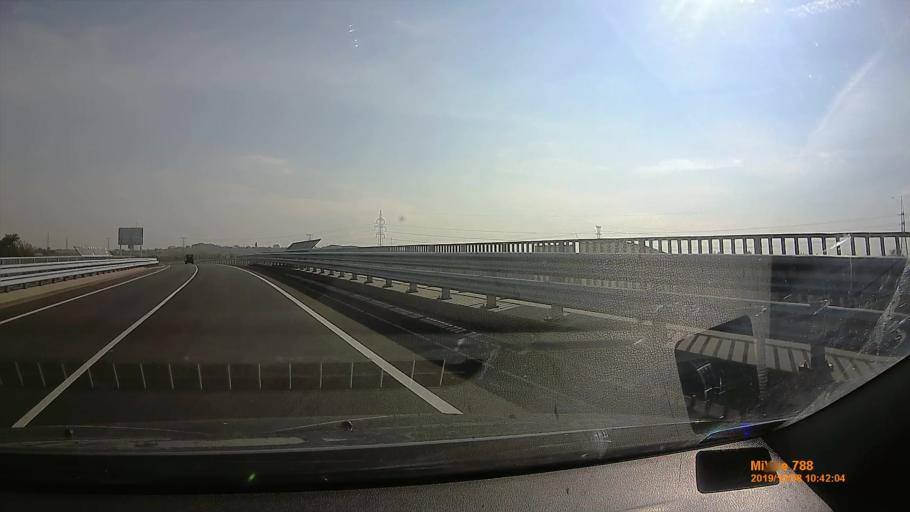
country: HU
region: Pest
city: God
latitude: 47.6640
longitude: 19.1317
